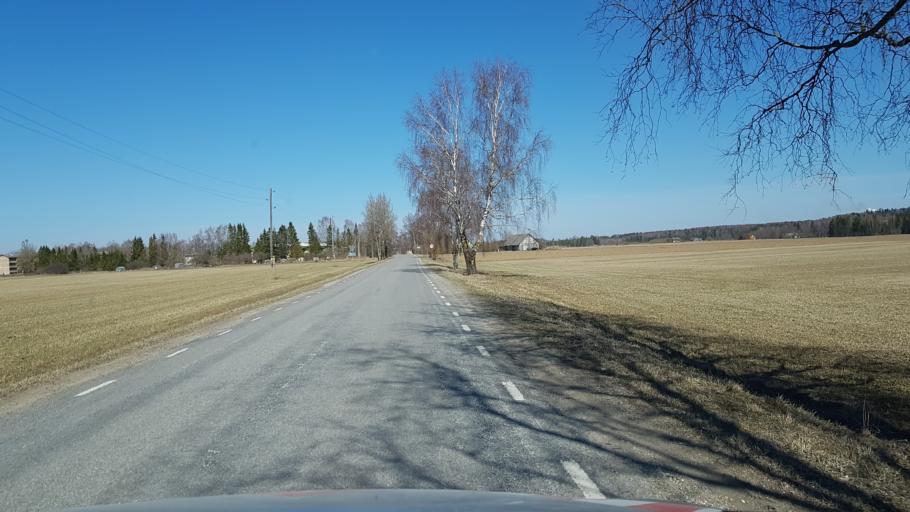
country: EE
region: Laeaene-Virumaa
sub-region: Vaeike-Maarja vald
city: Vaike-Maarja
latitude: 59.0940
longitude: 26.1948
